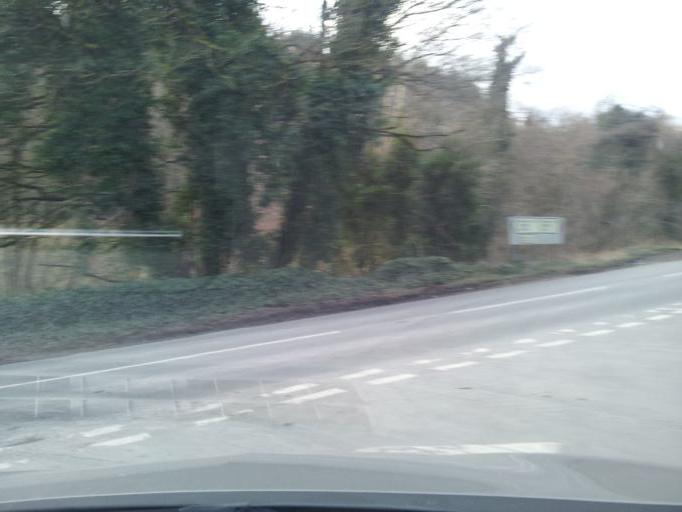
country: GB
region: England
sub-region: Derbyshire
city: Bakewell
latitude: 53.1610
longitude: -1.6557
